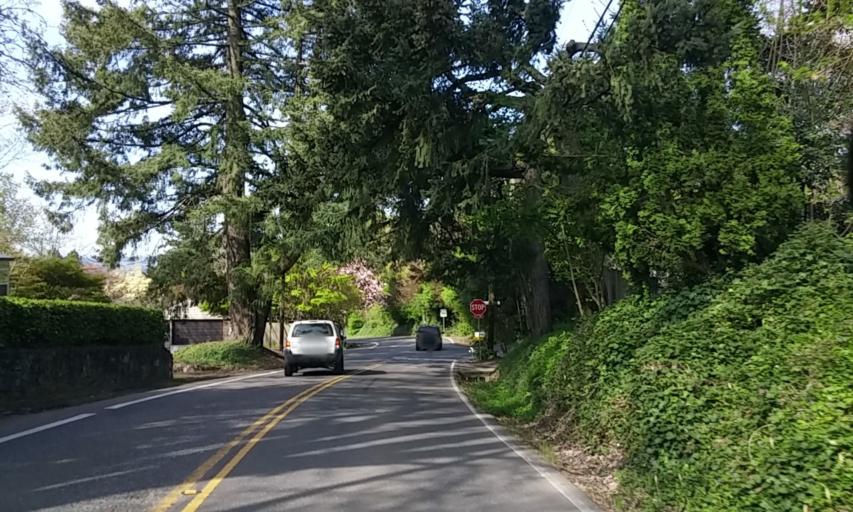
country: US
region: Oregon
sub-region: Washington County
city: West Slope
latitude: 45.5004
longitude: -122.7591
